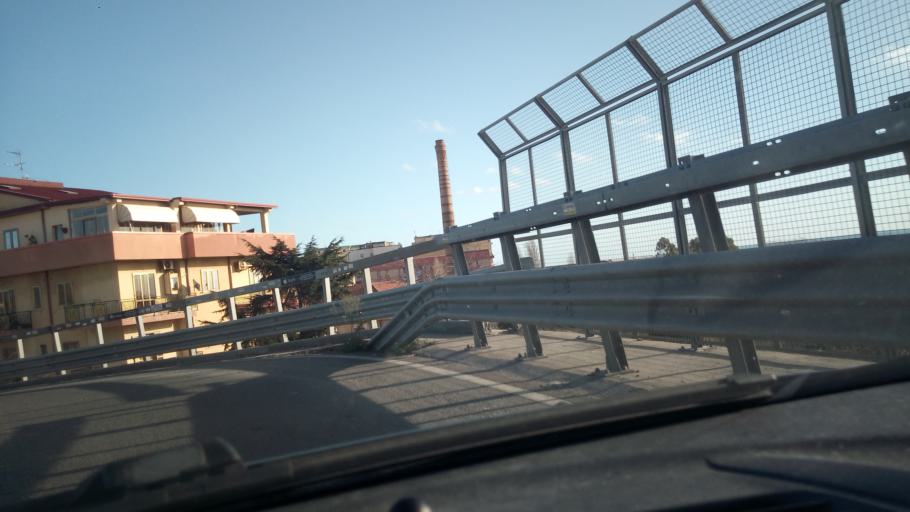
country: IT
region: Calabria
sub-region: Provincia di Catanzaro
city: Roccelletta
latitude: 38.8195
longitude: 16.6088
